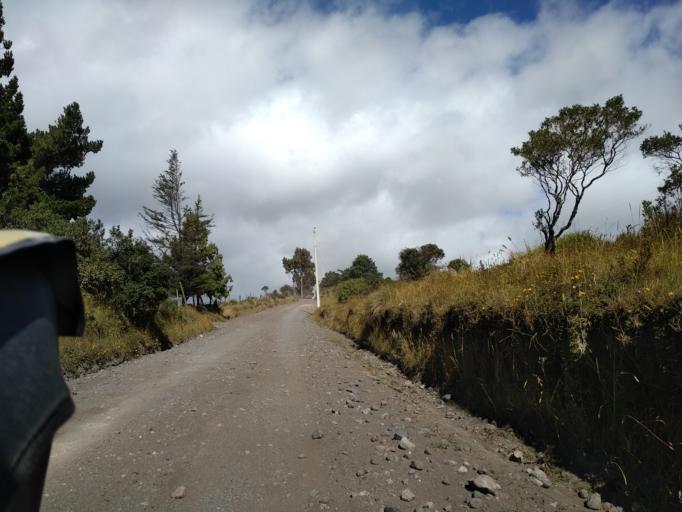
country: EC
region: Pichincha
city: Machachi
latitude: -0.5389
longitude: -78.4742
